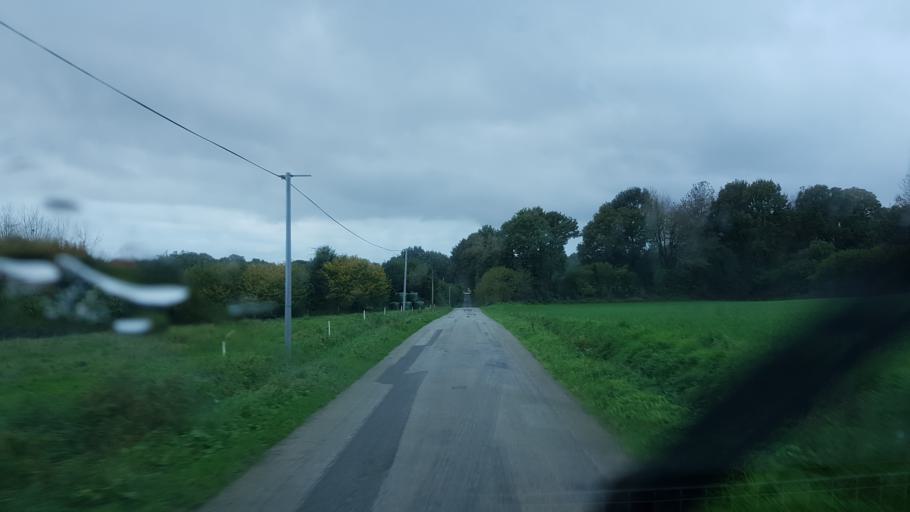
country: FR
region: Brittany
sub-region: Departement du Morbihan
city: Elven
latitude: 47.7454
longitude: -2.5589
